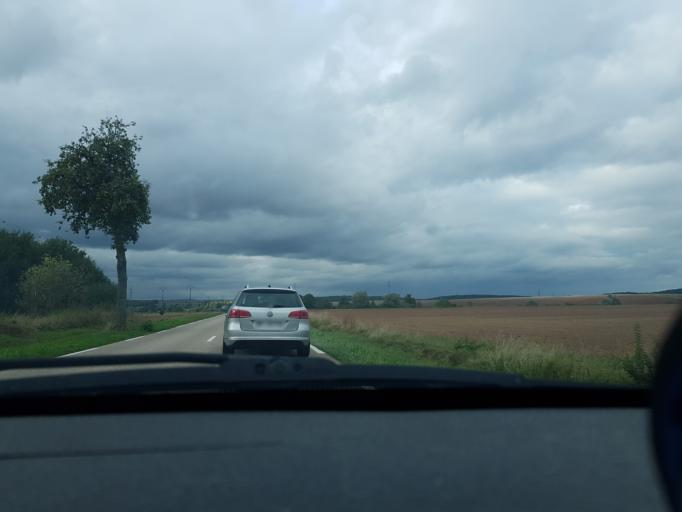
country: FR
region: Lorraine
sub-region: Departement de la Moselle
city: Morhange
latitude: 48.9494
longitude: 6.6111
